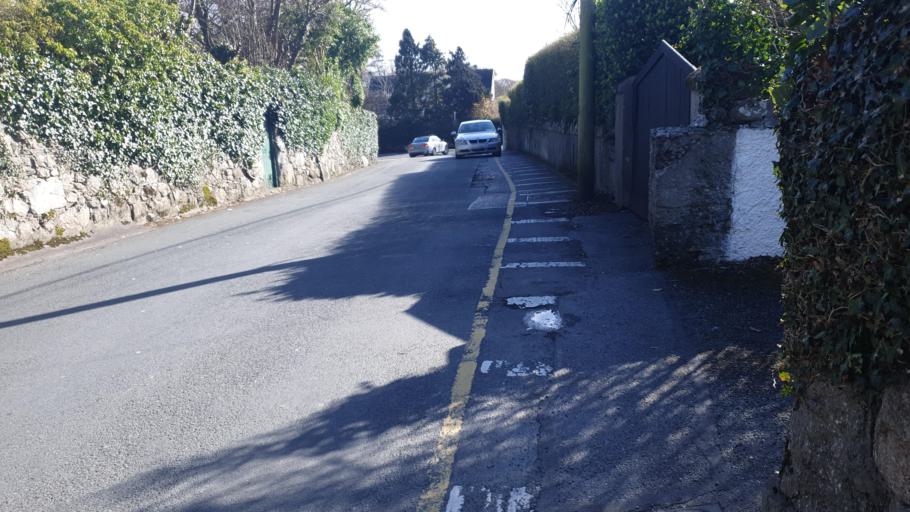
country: IE
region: Connaught
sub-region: County Galway
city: Gaillimh
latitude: 53.2693
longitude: -9.0718
